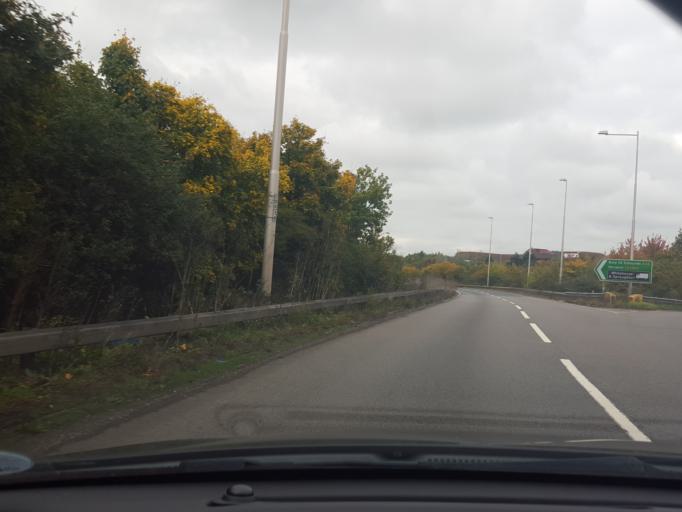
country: GB
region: England
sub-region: Suffolk
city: Bramford
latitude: 52.0358
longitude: 1.0973
